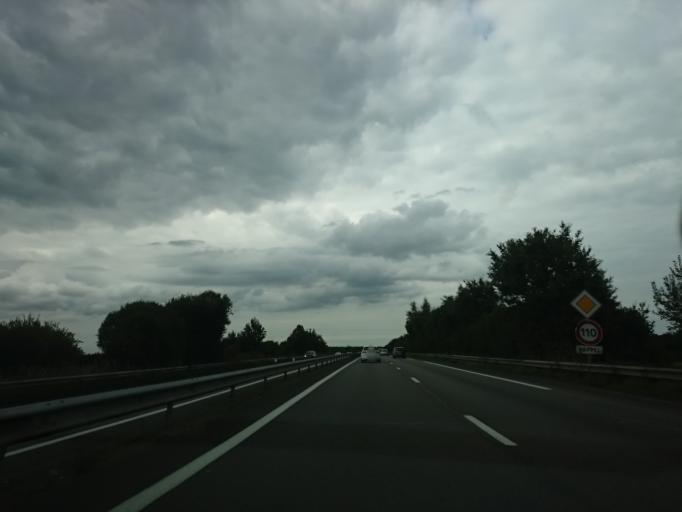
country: FR
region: Pays de la Loire
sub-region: Departement de la Loire-Atlantique
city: Treillieres
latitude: 47.3413
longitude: -1.6546
